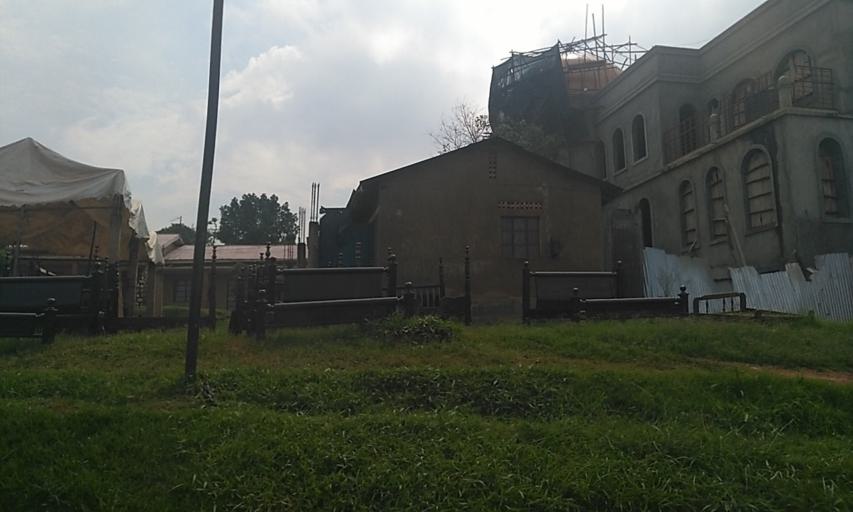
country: UG
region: Central Region
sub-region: Kampala District
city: Kampala
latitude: 0.2761
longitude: 32.5654
